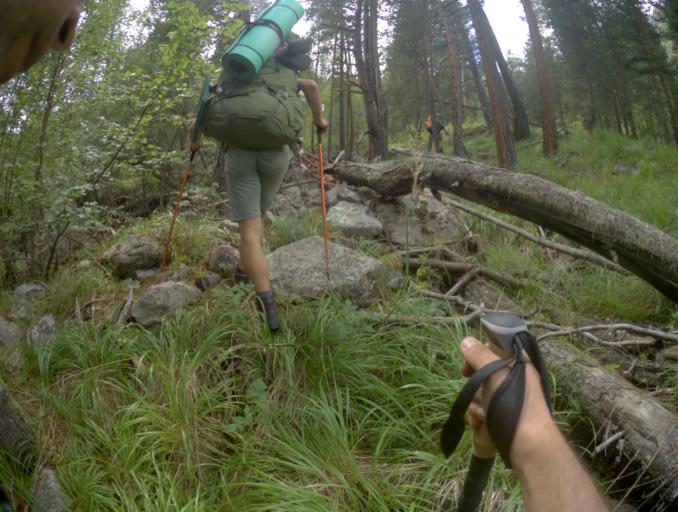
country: RU
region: Karachayevo-Cherkesiya
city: Uchkulan
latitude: 43.3494
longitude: 42.1543
